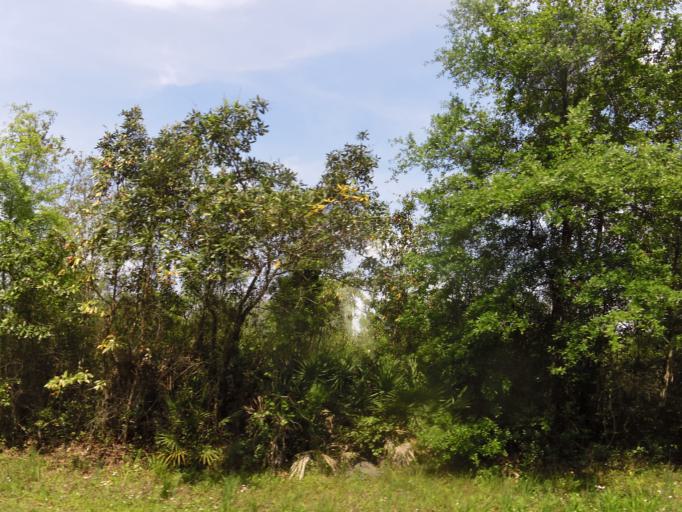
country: US
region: Georgia
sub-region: Camden County
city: Kingsland
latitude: 30.7883
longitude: -81.7137
